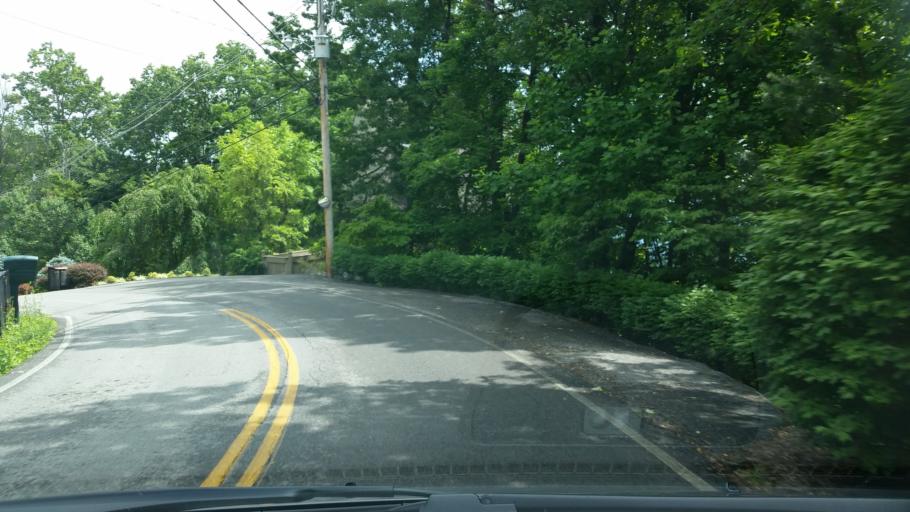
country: US
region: Tennessee
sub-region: Sevier County
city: Gatlinburg
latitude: 35.7075
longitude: -83.5585
